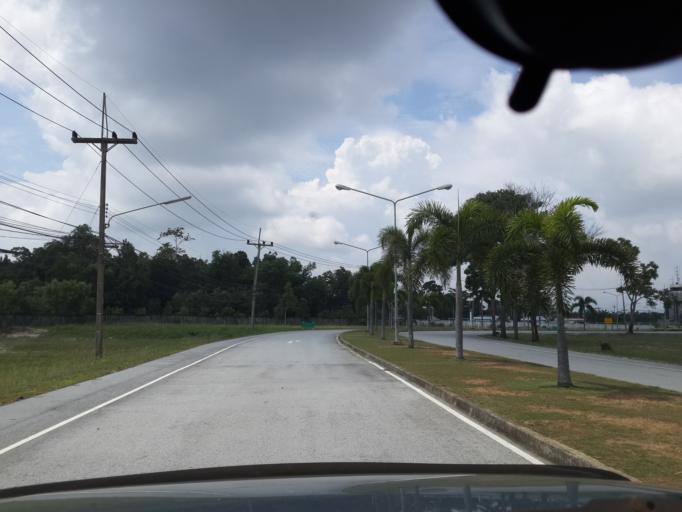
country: TH
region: Narathiwat
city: Bacho
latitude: 6.5216
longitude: 101.7502
